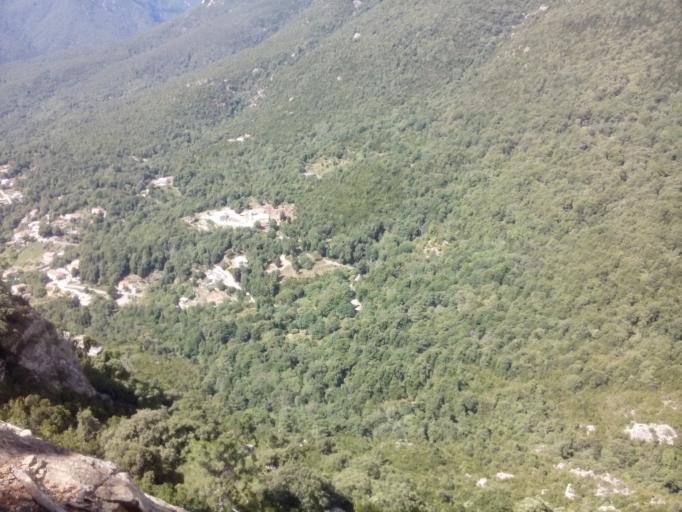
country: FR
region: Corsica
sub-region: Departement de la Haute-Corse
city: Ventiseri
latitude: 41.9300
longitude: 9.2715
